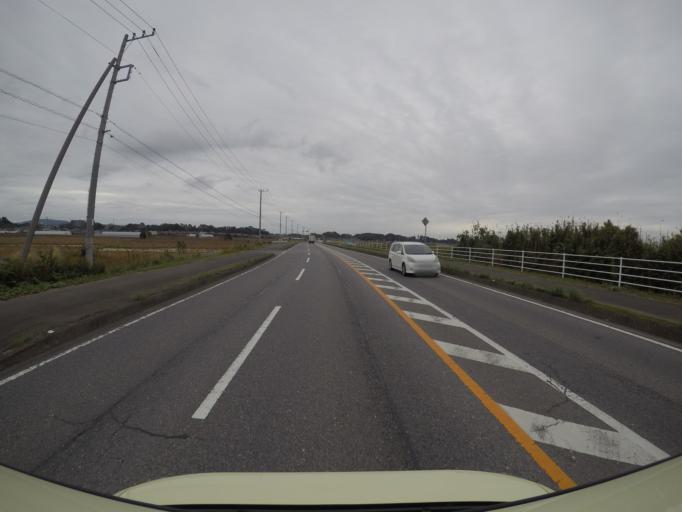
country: JP
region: Ibaraki
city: Ami
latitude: 36.0904
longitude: 140.2203
